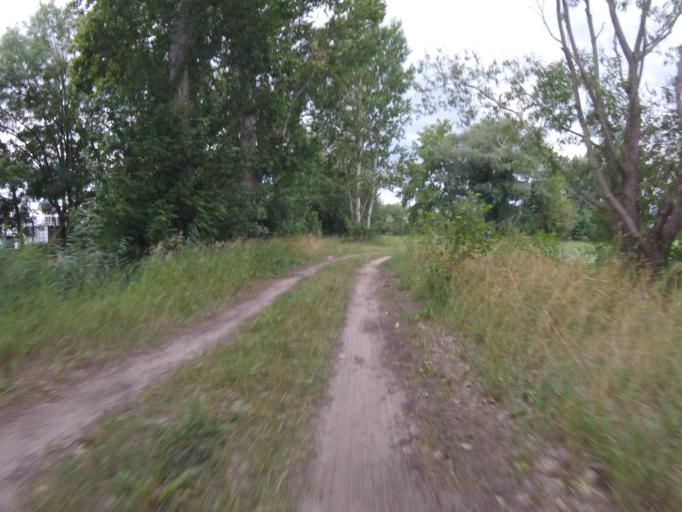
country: DE
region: Brandenburg
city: Mittenwalde
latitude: 52.2722
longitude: 13.5318
